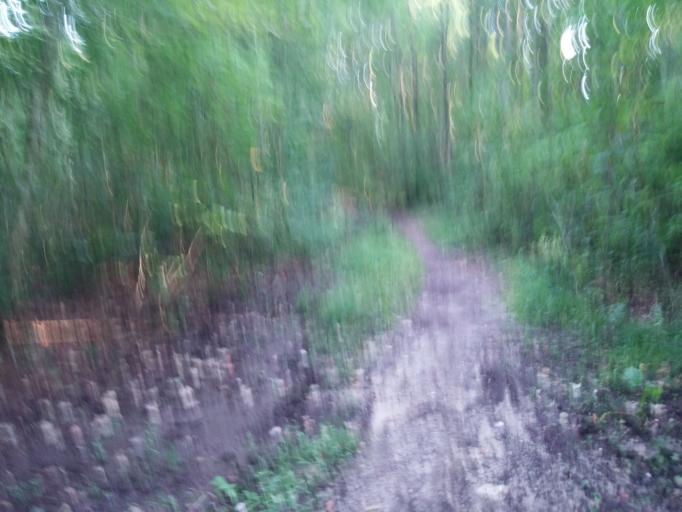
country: DE
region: Bavaria
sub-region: Upper Bavaria
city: Kirchseeon
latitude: 48.0847
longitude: 11.8696
